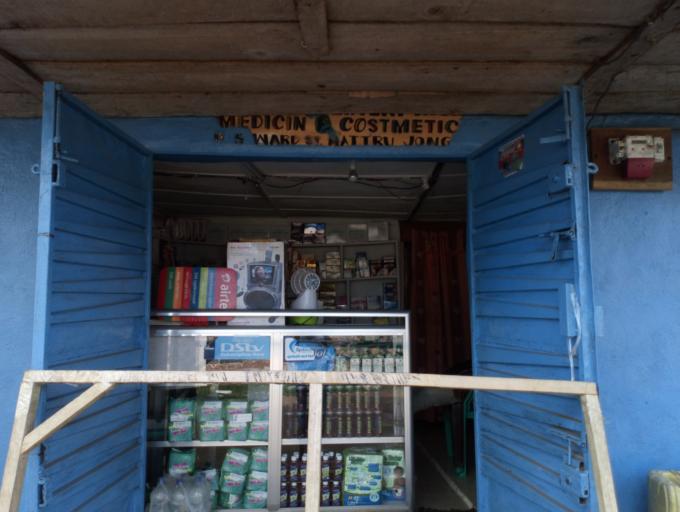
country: SL
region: Southern Province
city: Mogbwemo
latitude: 7.6060
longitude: -12.1782
